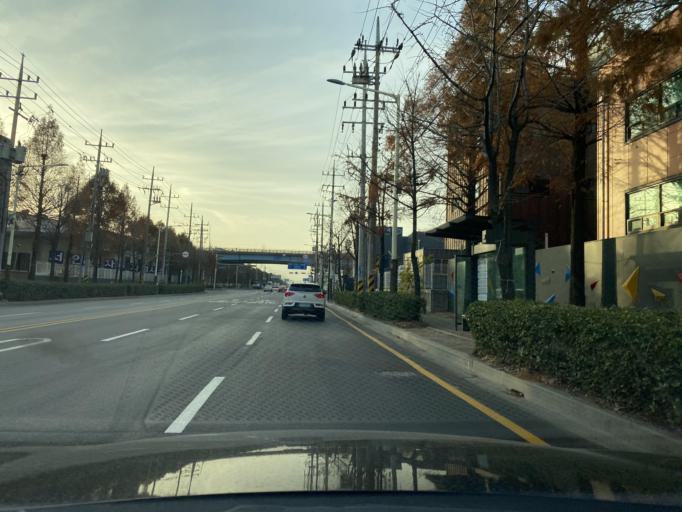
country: KR
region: Incheon
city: Incheon
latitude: 37.4993
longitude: 126.6499
